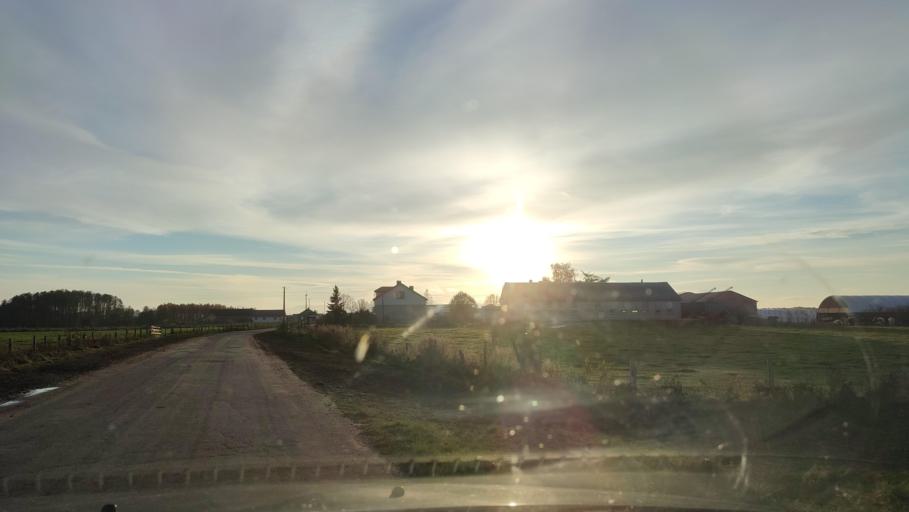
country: PL
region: Masovian Voivodeship
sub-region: Powiat mlawski
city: Dzierzgowo
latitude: 53.2833
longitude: 20.6535
